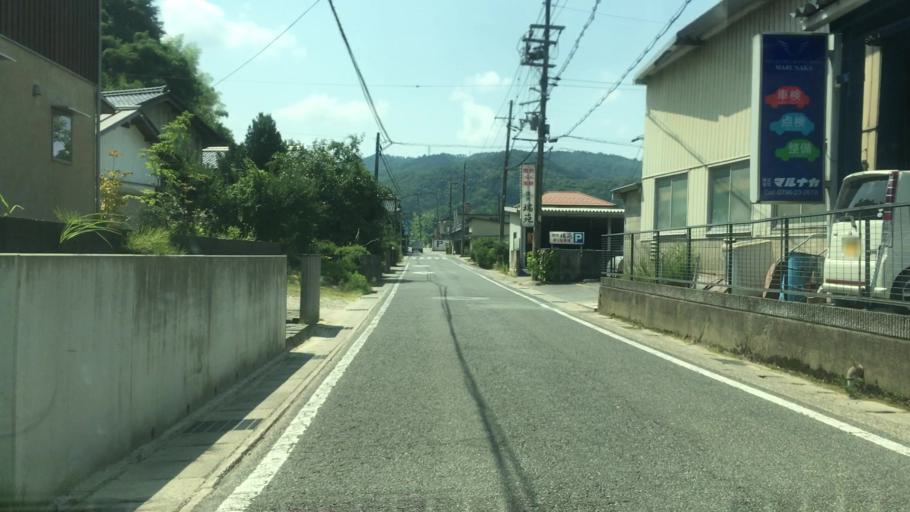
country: JP
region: Hyogo
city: Toyooka
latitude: 35.5552
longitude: 134.7971
